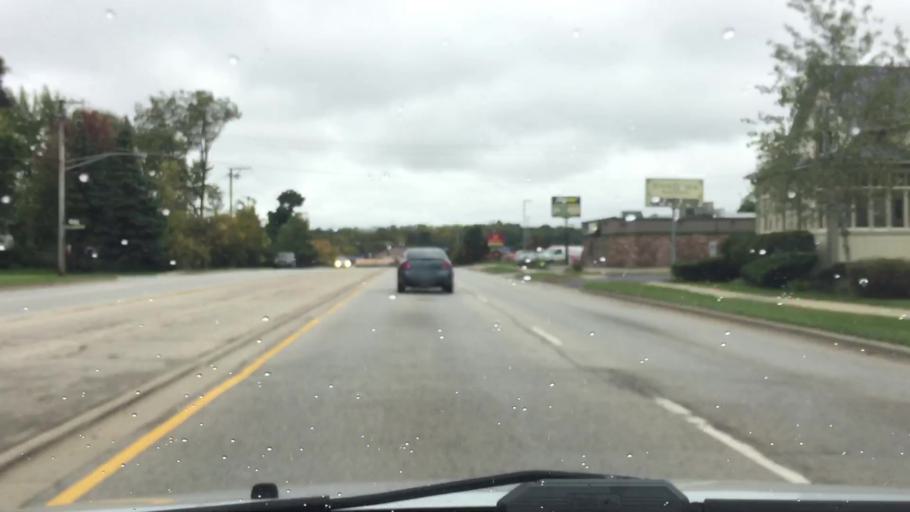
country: US
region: Illinois
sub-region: Kane County
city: West Dundee
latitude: 42.0955
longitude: -88.2872
